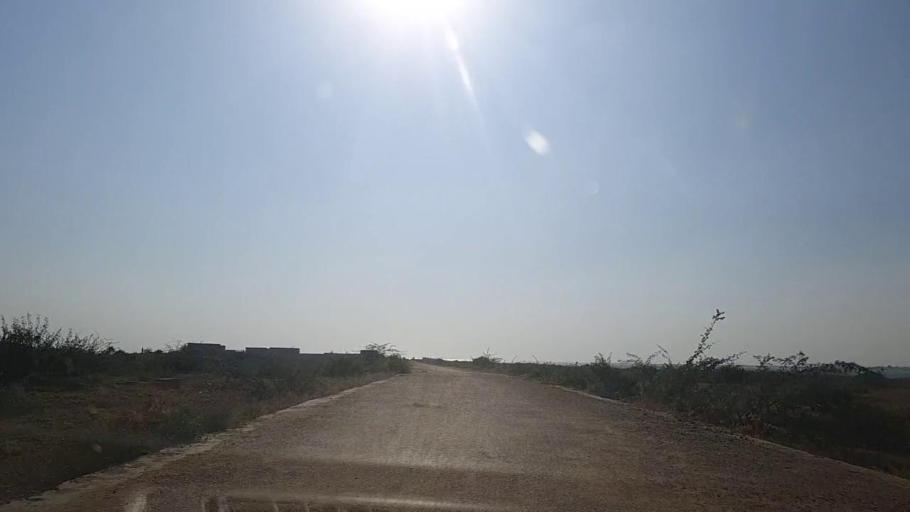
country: PK
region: Sindh
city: Daro Mehar
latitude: 25.0056
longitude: 68.1155
